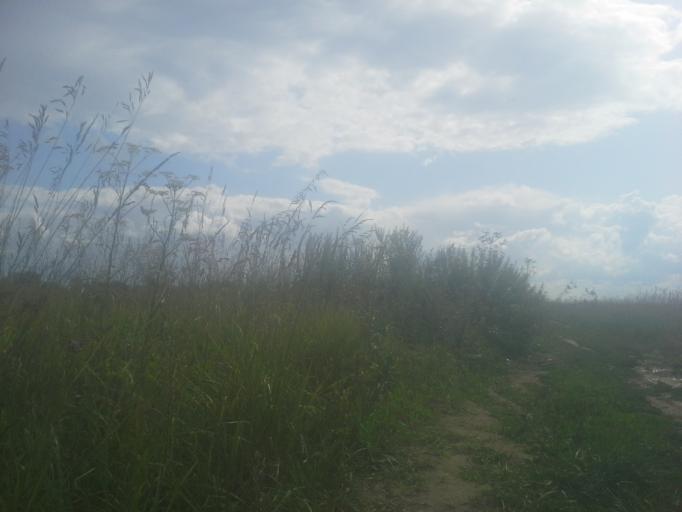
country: RU
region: Moskovskaya
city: Zhavoronki
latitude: 55.6507
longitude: 37.1400
